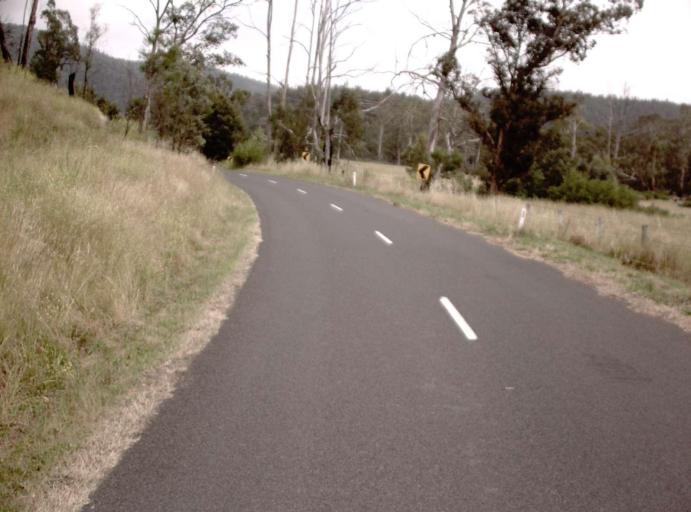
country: AU
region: Victoria
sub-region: Wellington
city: Heyfield
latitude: -37.7910
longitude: 146.6790
